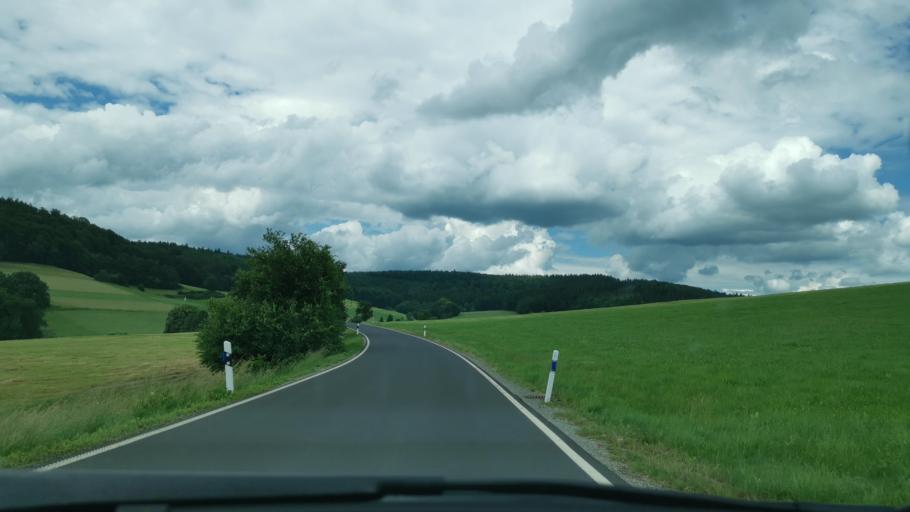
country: DE
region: Hesse
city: Hessisch Lichtenau
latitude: 51.1481
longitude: 9.7342
